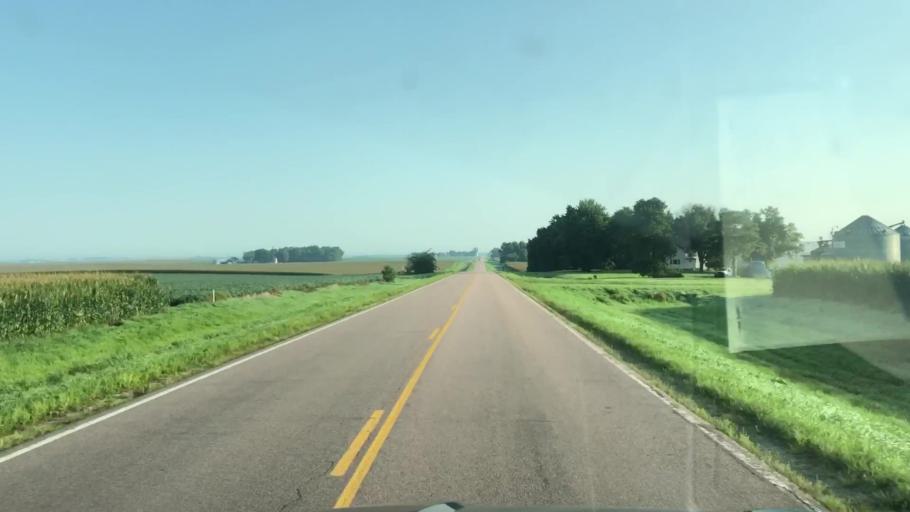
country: US
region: Iowa
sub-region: Lyon County
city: George
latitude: 43.2919
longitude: -95.9995
